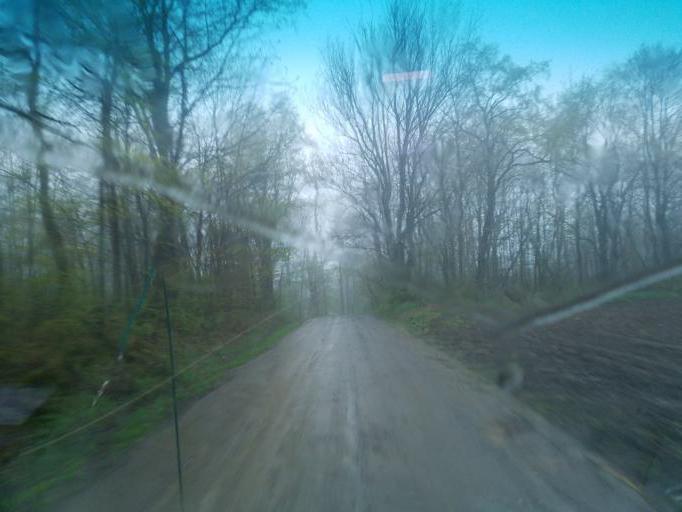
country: US
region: Pennsylvania
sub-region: Tioga County
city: Westfield
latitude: 41.9328
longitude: -77.7186
